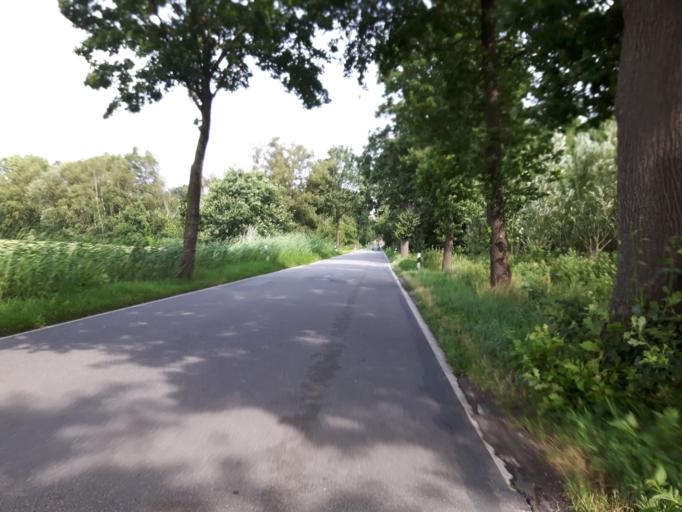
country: DE
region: Lower Saxony
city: Ovelgonne
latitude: 53.2709
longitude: 8.3340
